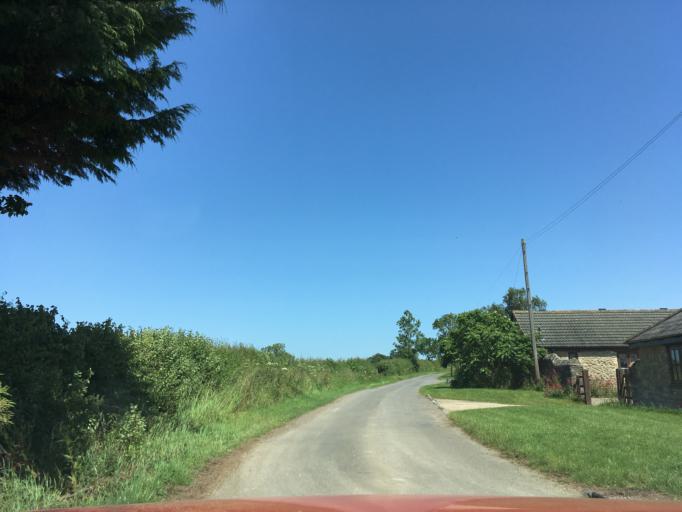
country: GB
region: England
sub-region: Northamptonshire
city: Brackley
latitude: 52.0144
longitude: -1.0719
